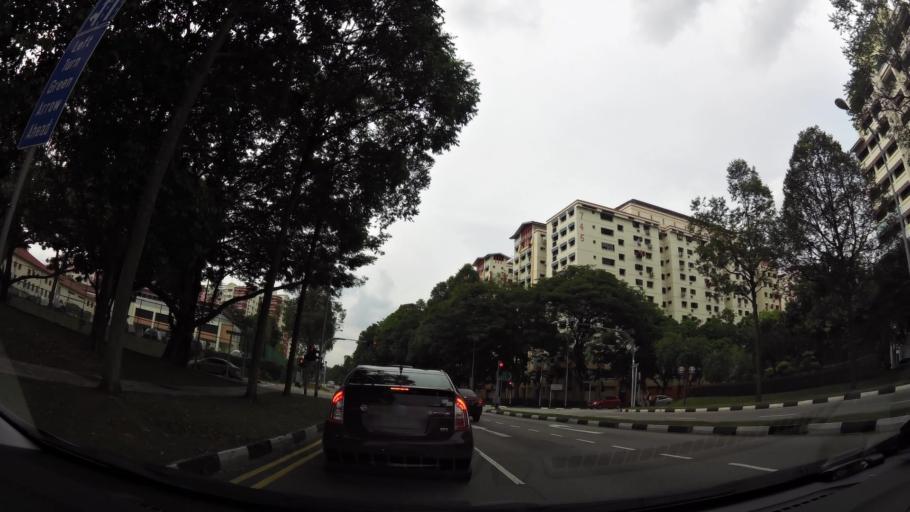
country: MY
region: Johor
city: Johor Bahru
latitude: 1.4413
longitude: 103.7954
